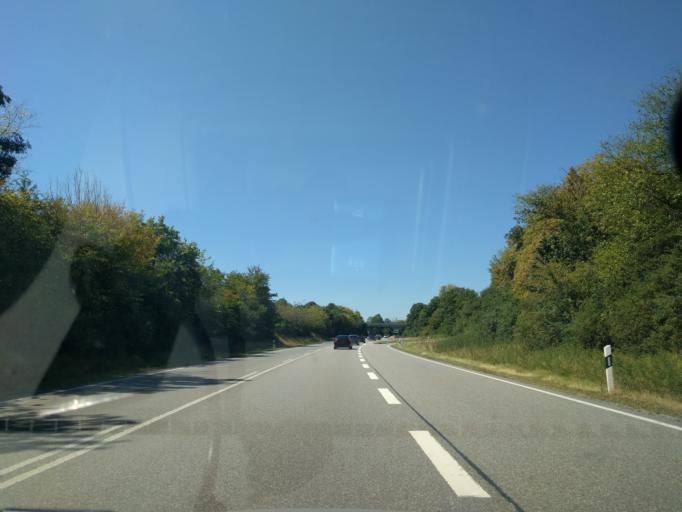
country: DE
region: Bavaria
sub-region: Upper Bavaria
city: Fuerstenfeldbruck
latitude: 48.1860
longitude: 11.2467
